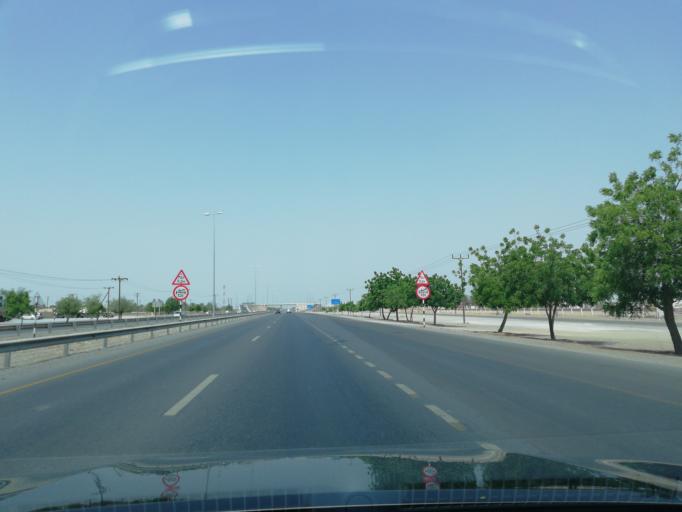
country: OM
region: Al Batinah
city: Barka'
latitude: 23.6749
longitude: 57.9897
